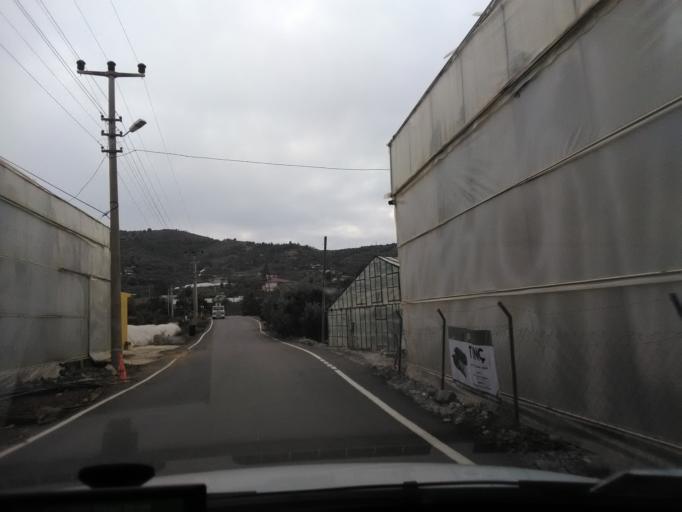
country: TR
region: Antalya
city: Gazipasa
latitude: 36.2515
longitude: 32.3417
